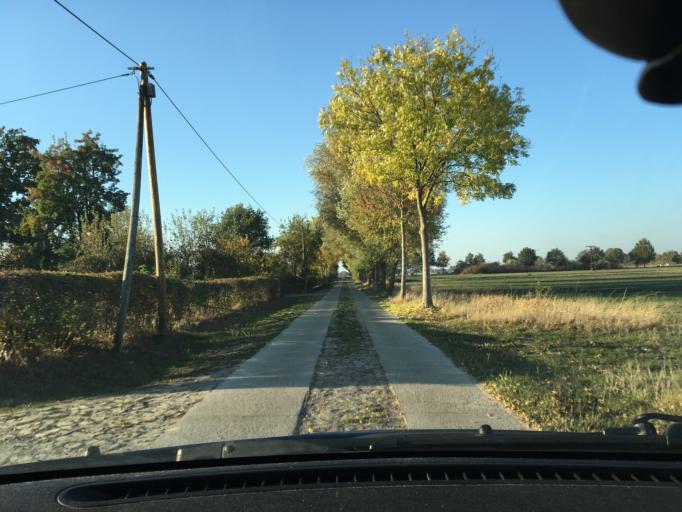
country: DE
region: Lower Saxony
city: Bleckede
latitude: 53.2873
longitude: 10.8060
